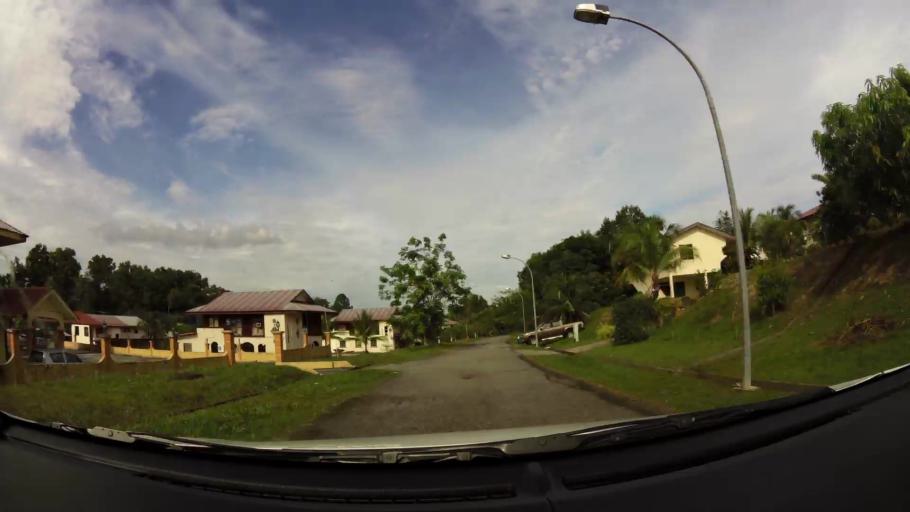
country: BN
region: Brunei and Muara
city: Bandar Seri Begawan
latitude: 4.8956
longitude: 114.8870
